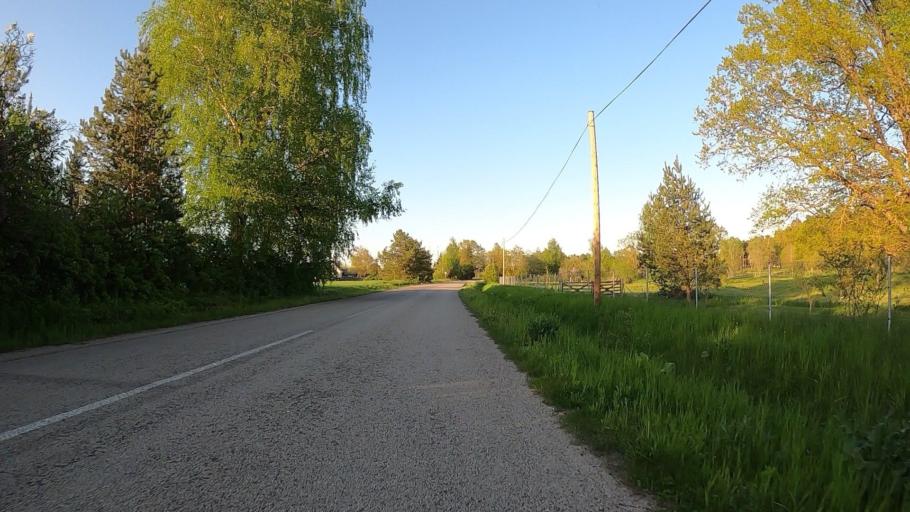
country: LV
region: Kekava
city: Kekava
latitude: 56.8149
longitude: 24.2066
